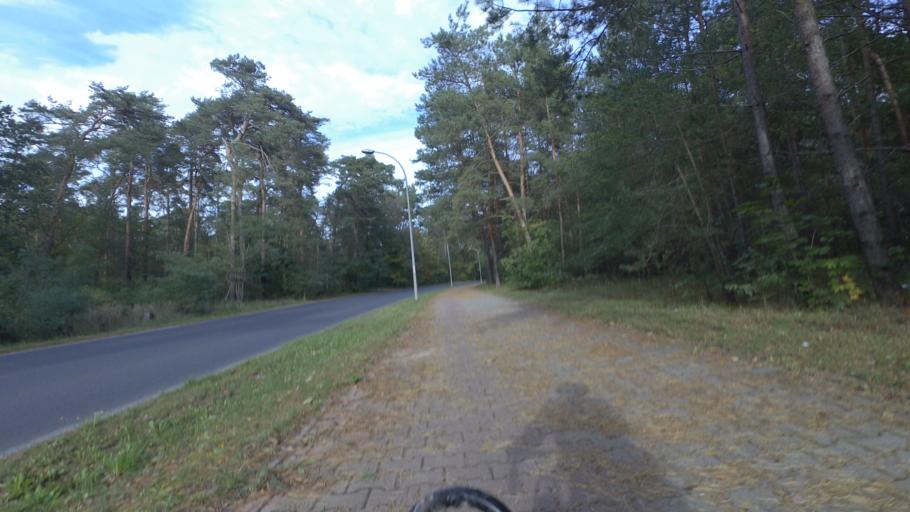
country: DE
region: Brandenburg
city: Ludwigsfelde
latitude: 52.3147
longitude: 13.2496
